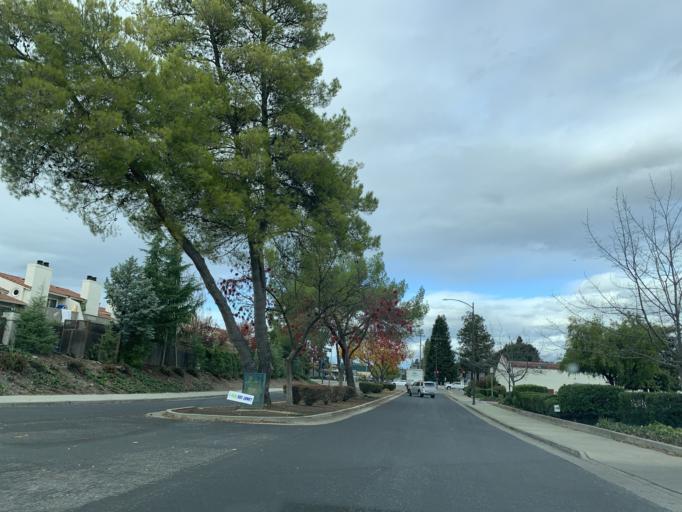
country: US
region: California
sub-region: Santa Clara County
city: Monte Sereno
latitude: 37.2633
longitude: -121.9852
